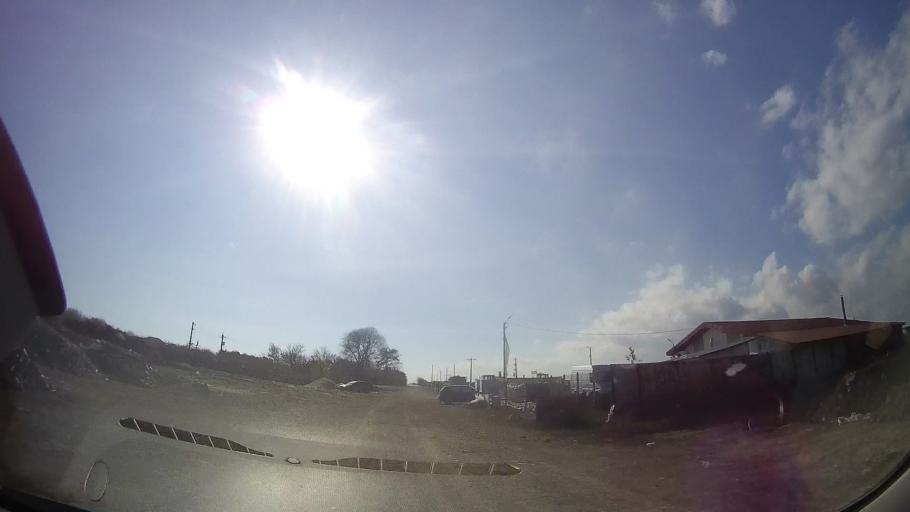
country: RO
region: Constanta
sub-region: Comuna Costinesti
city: Costinesti
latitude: 43.9634
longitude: 28.6378
